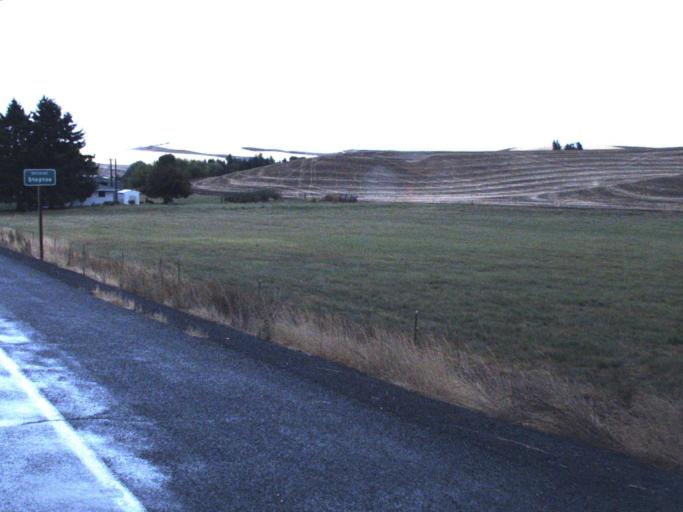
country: US
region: Washington
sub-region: Whitman County
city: Colfax
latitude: 47.0042
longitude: -117.3602
